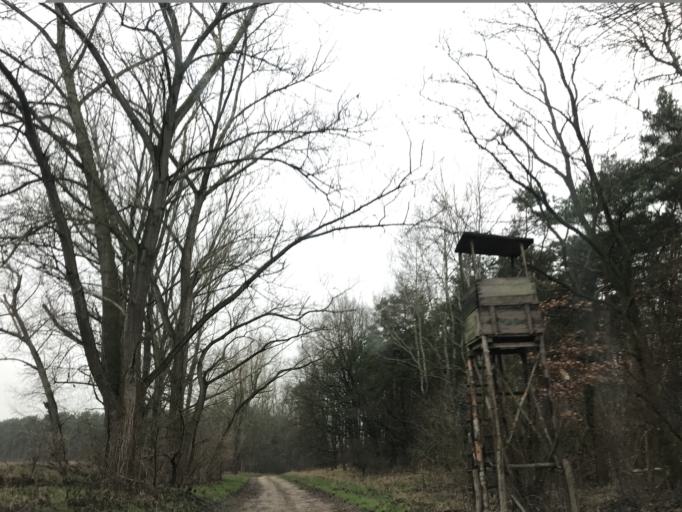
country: DE
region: Brandenburg
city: Kremmen
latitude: 52.7483
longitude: 12.9745
